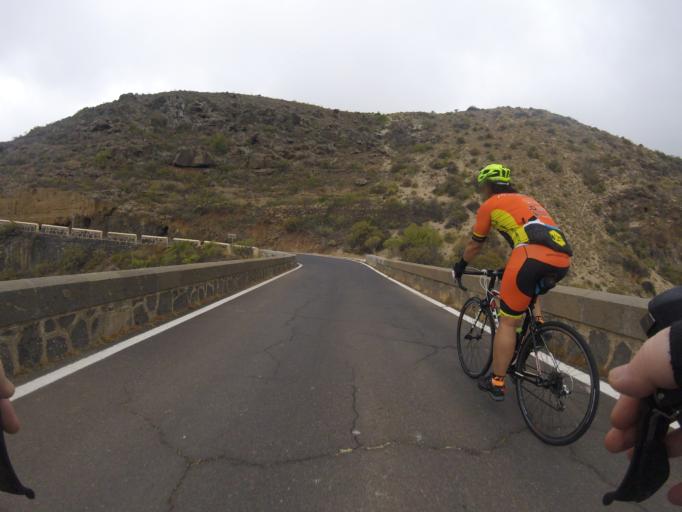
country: ES
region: Canary Islands
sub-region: Provincia de Santa Cruz de Tenerife
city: Fasnia
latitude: 28.2174
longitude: -16.4527
